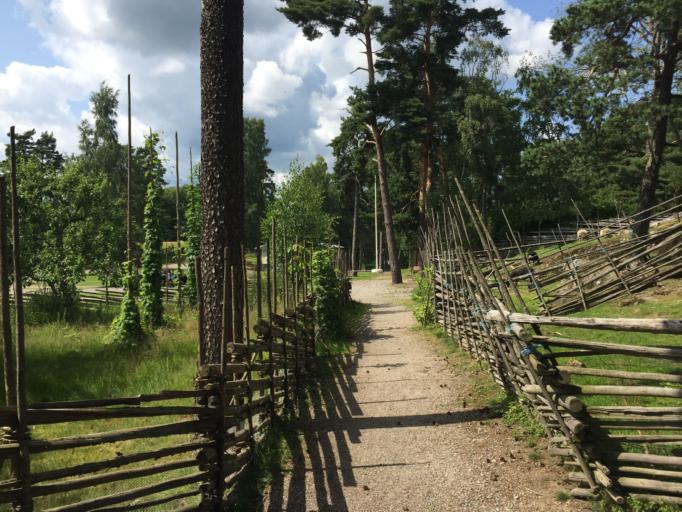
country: SE
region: Stockholm
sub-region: Sodertalje Kommun
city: Soedertaelje
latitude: 59.1920
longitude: 17.6155
